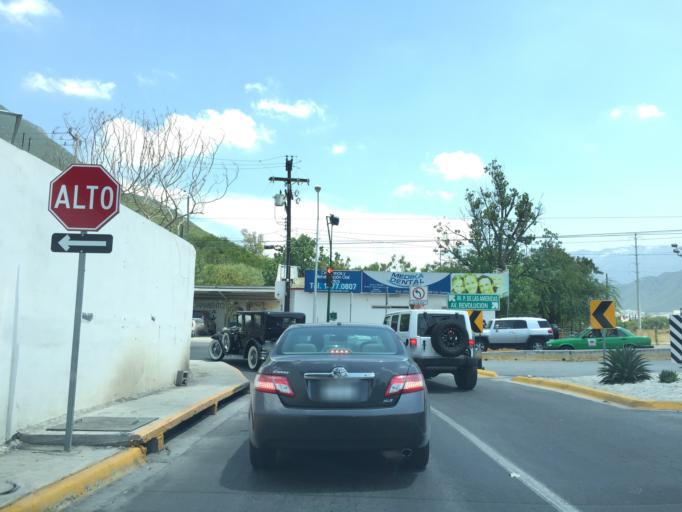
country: MX
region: Nuevo Leon
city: Guadalupe
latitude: 25.6396
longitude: -100.2684
